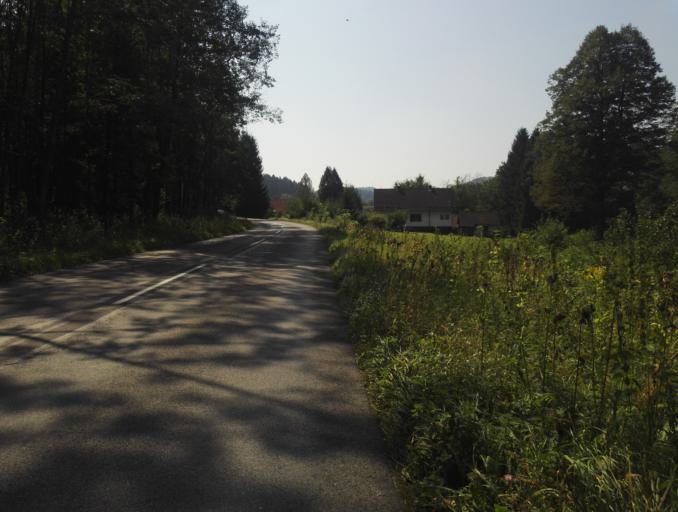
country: AT
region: Styria
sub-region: Politischer Bezirk Graz-Umgebung
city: Gratwein
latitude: 47.1122
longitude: 15.2994
